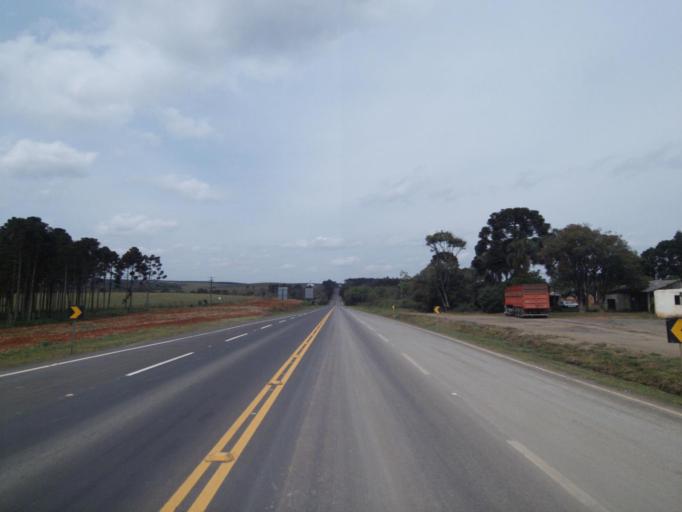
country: BR
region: Parana
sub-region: Irati
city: Irati
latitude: -25.4639
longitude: -50.5597
